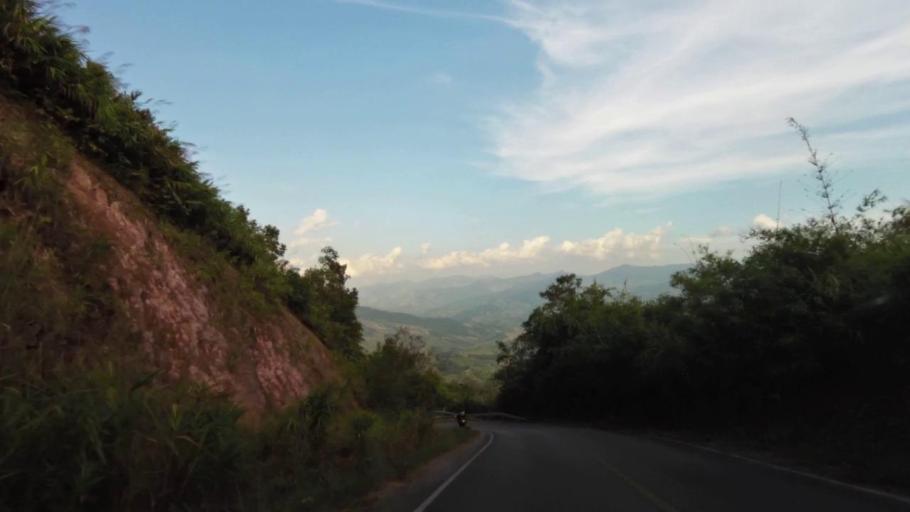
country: TH
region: Chiang Rai
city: Khun Tan
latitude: 19.8733
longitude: 100.3495
